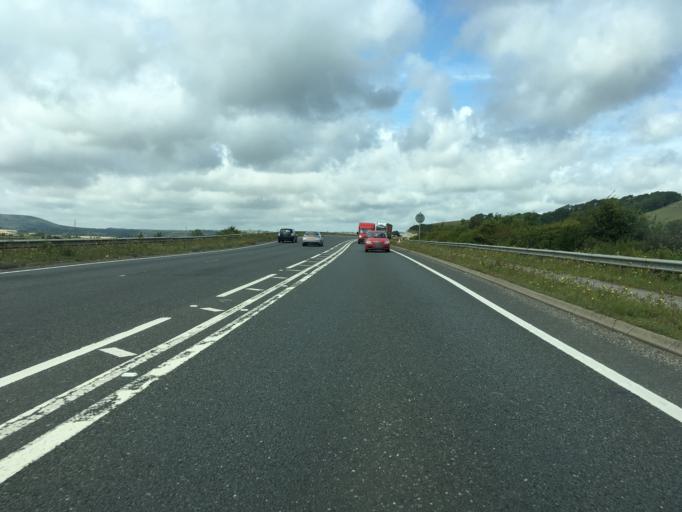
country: GB
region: England
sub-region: East Sussex
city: Ringmer
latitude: 50.8552
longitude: 0.0488
